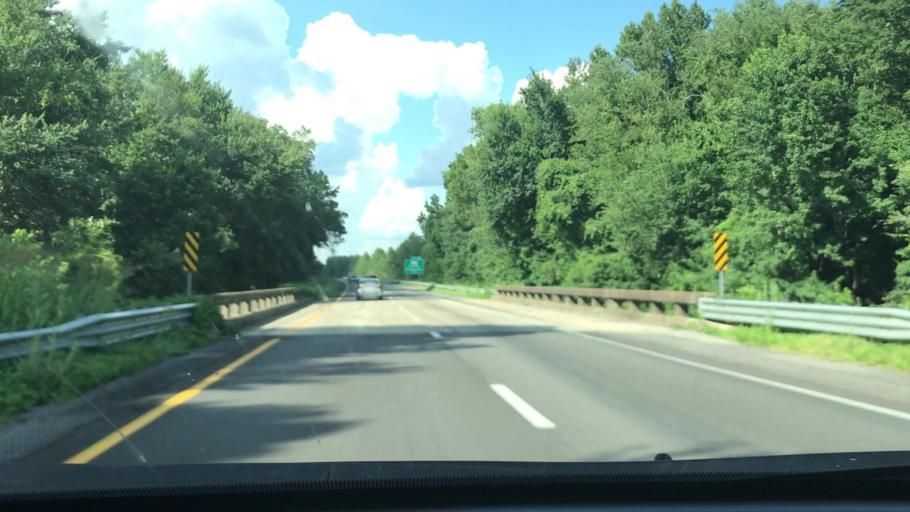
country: US
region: South Carolina
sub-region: Clarendon County
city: Manning
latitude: 33.8428
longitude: -80.1234
